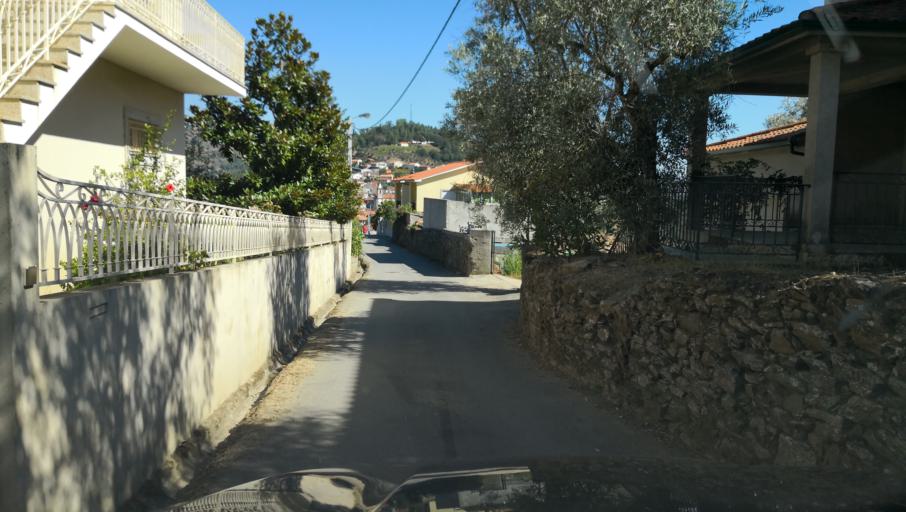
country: PT
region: Vila Real
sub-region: Santa Marta de Penaguiao
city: Santa Marta de Penaguiao
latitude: 41.2461
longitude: -7.8153
